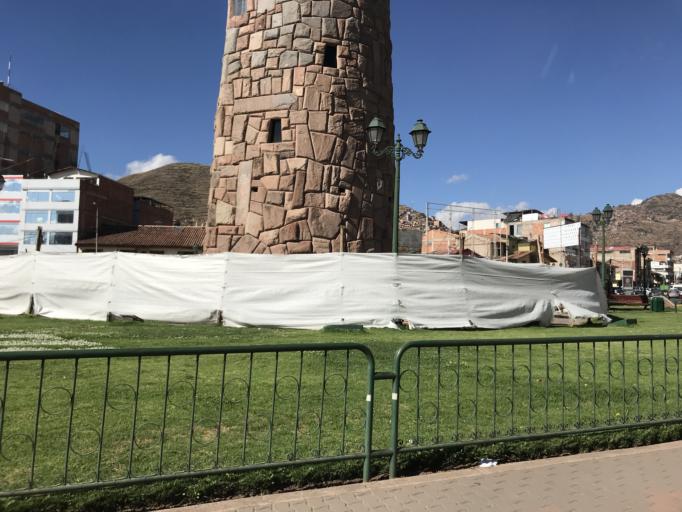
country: PE
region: Cusco
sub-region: Provincia de Cusco
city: Cusco
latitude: -13.5316
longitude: -71.9682
